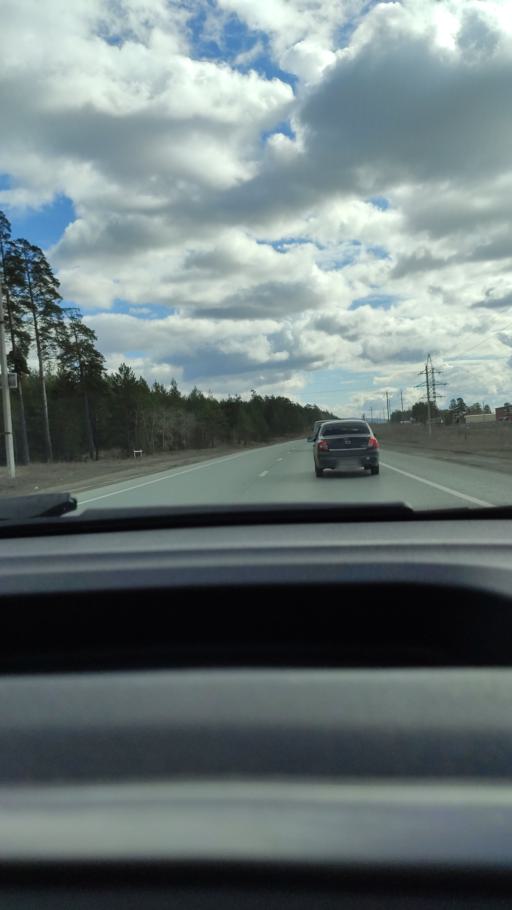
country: RU
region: Samara
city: Kurumoch
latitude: 53.4733
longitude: 50.0632
